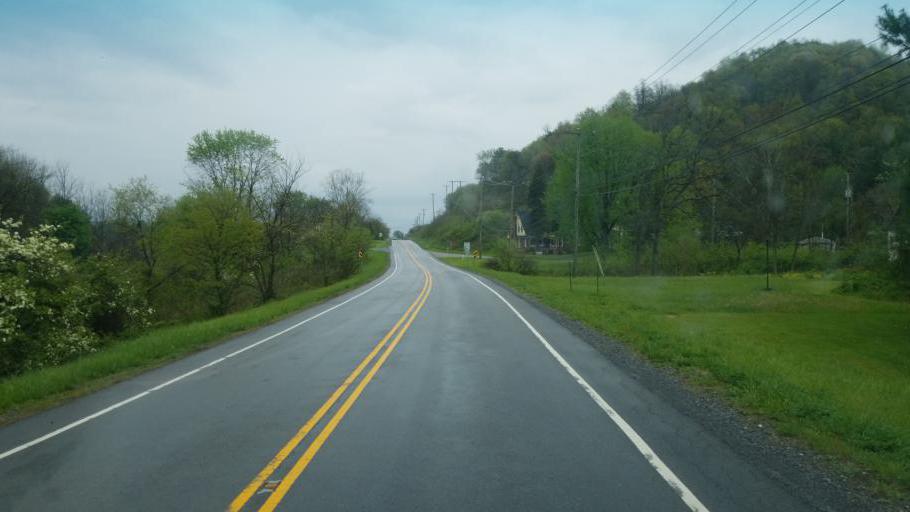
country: US
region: Virginia
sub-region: Smyth County
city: Atkins
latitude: 36.8787
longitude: -81.3837
